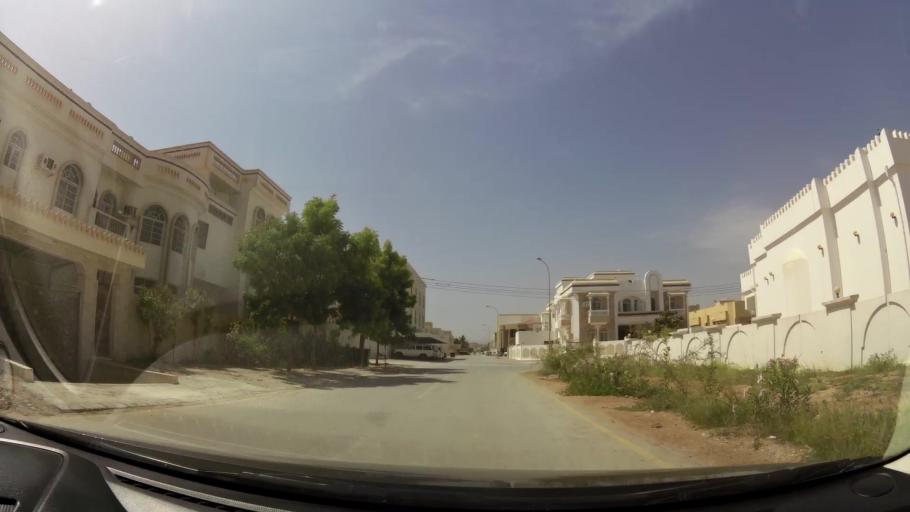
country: OM
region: Zufar
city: Salalah
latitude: 17.0423
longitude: 54.1495
